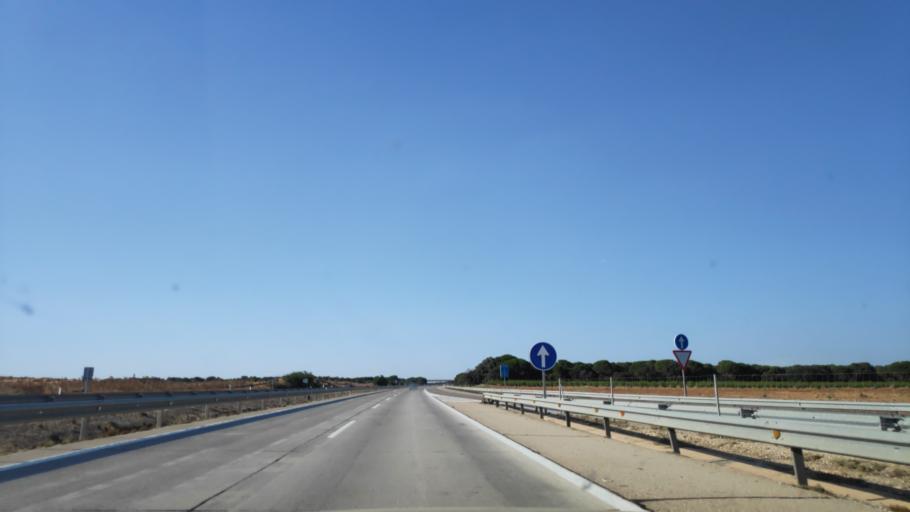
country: ES
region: Castille-La Mancha
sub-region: Provincia de Cuenca
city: Pozoamargo
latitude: 39.3236
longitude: -2.2028
